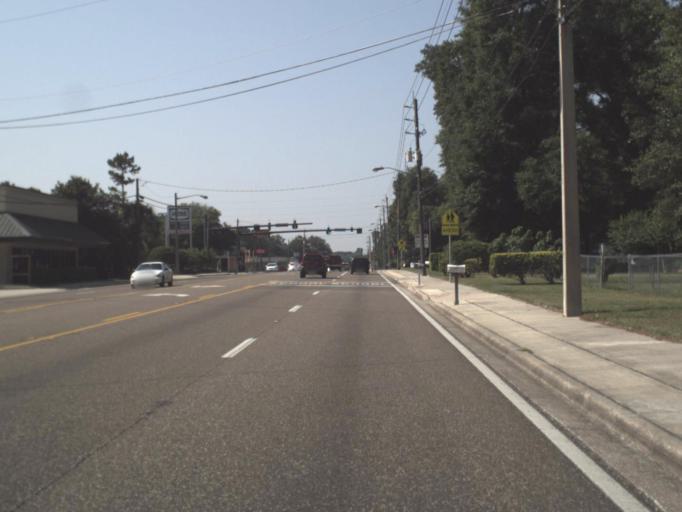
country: US
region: Florida
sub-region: Clay County
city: Bellair-Meadowbrook Terrace
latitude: 30.2860
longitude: -81.7554
